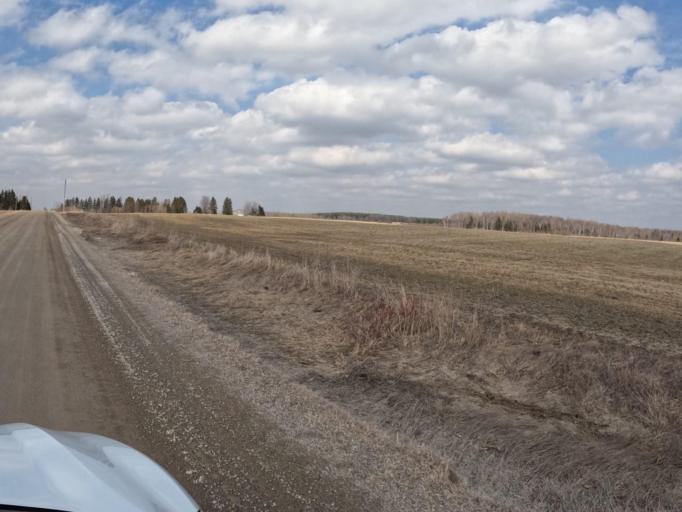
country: CA
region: Ontario
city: Shelburne
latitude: 43.9725
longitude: -80.2674
